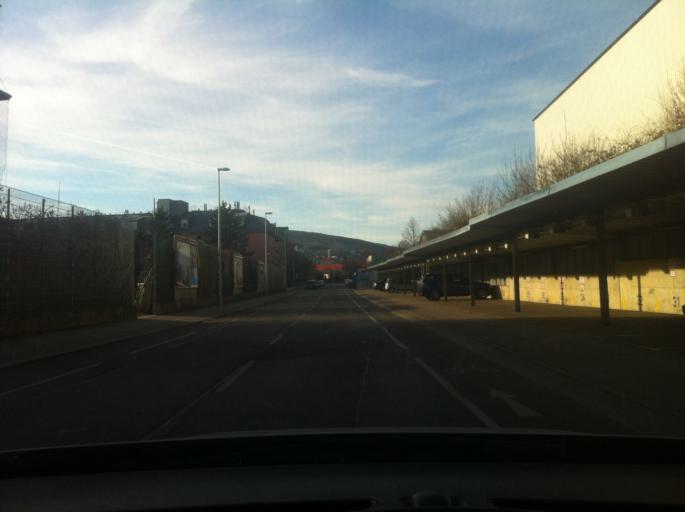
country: AT
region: Lower Austria
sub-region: Politischer Bezirk Modling
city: Perchtoldsdorf
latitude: 48.1923
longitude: 16.2907
